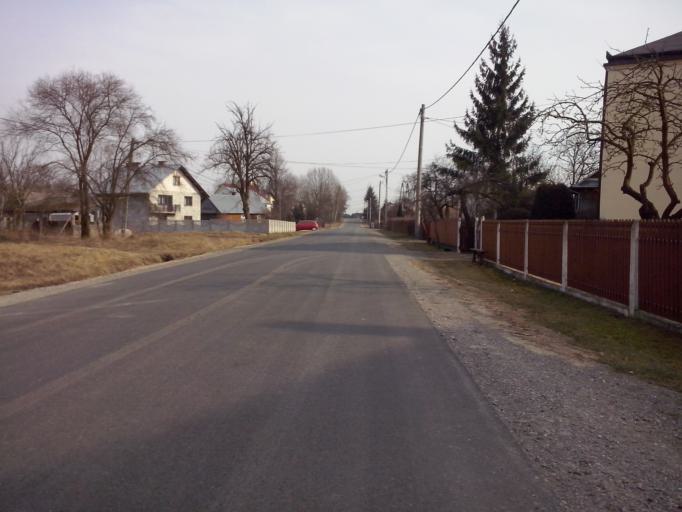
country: PL
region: Subcarpathian Voivodeship
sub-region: Powiat nizanski
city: Krzeszow
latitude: 50.4249
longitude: 22.3559
